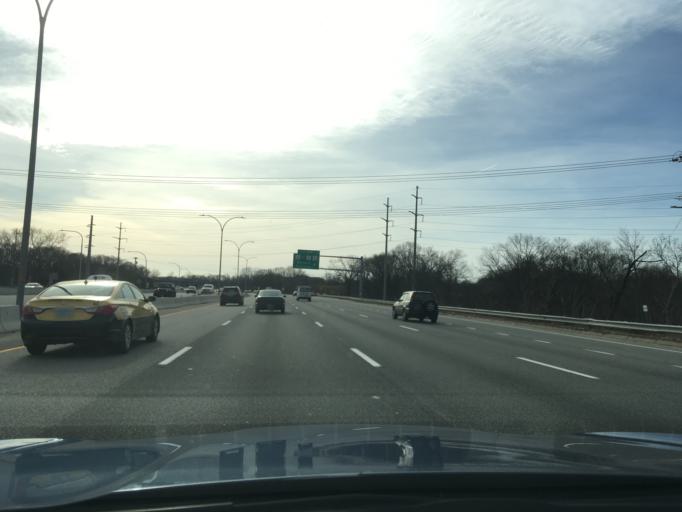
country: US
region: Rhode Island
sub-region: Providence County
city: Cranston
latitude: 41.7527
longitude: -71.4392
